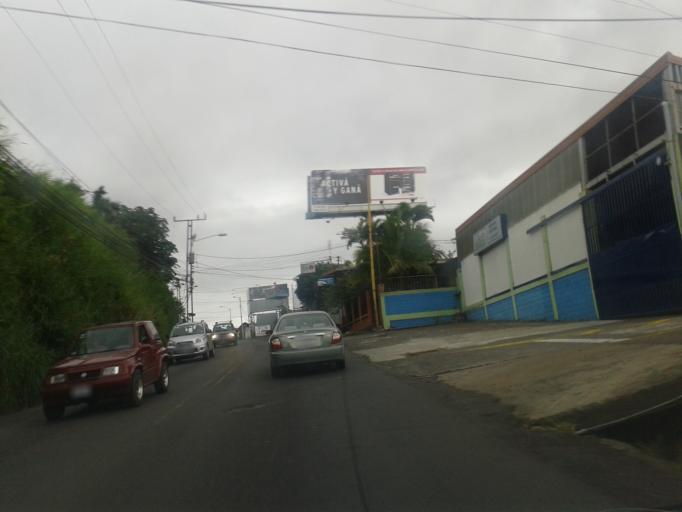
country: CR
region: Heredia
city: San Pablo
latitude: 9.9879
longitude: -84.0979
